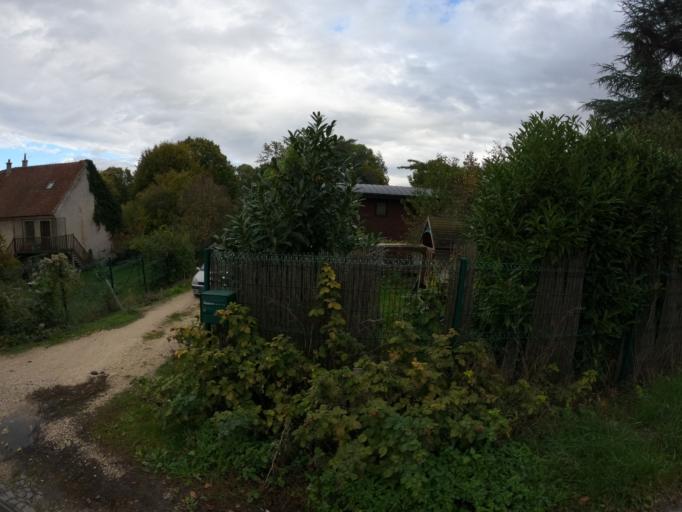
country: FR
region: Ile-de-France
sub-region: Departement de Seine-et-Marne
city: Saint-Germain-sur-Morin
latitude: 48.8735
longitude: 2.8434
